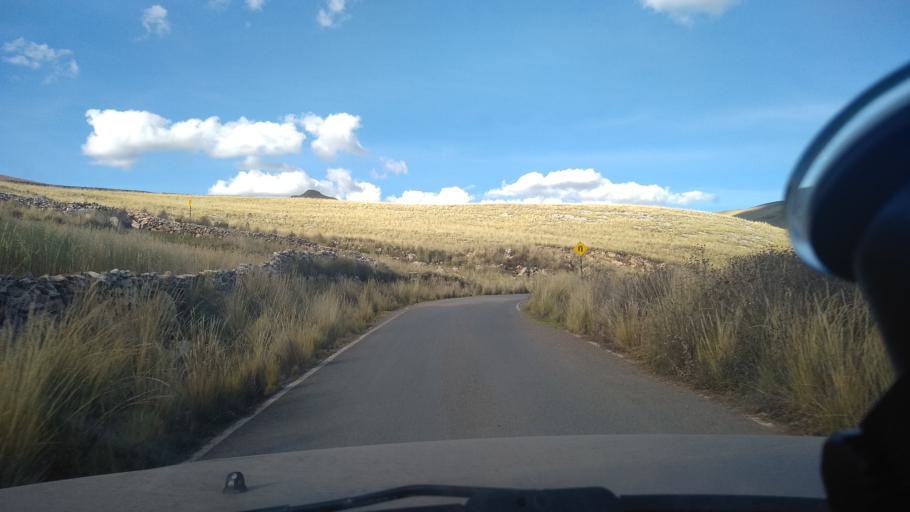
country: PE
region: Cusco
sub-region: Provincia de Canas
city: Cahuanuyo
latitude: -14.3426
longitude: -71.4467
